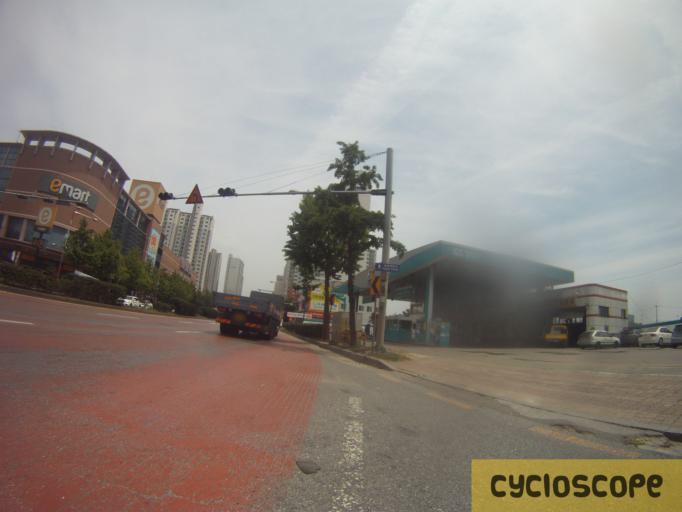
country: KR
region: Incheon
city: Incheon
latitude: 37.4653
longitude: 126.6334
